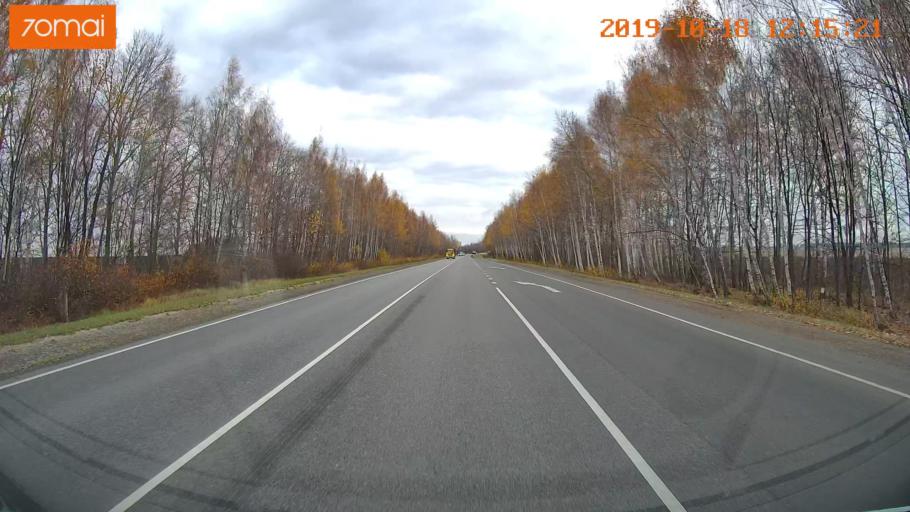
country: RU
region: Rjazan
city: Zakharovo
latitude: 54.4424
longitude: 39.3988
